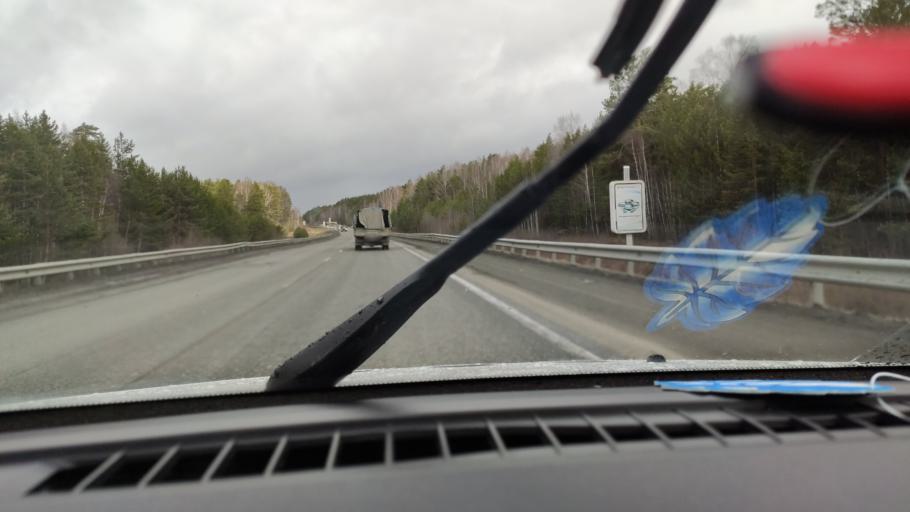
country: RU
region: Sverdlovsk
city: Talitsa
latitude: 56.8678
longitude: 60.0444
